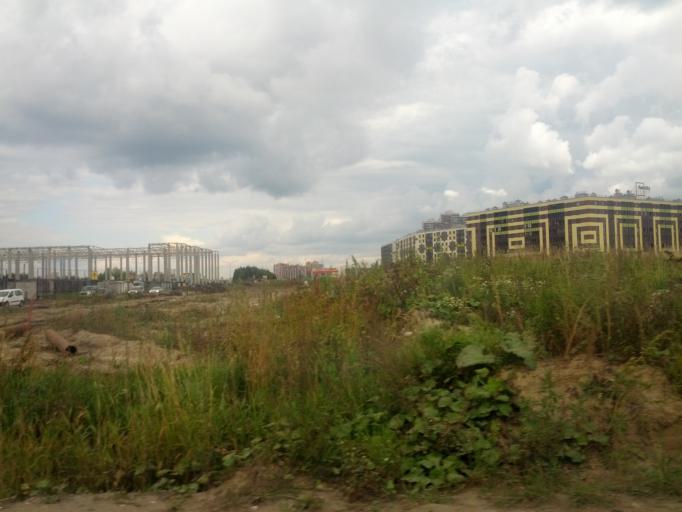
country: RU
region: Leningrad
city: Rybatskoye
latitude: 59.8938
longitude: 30.5045
